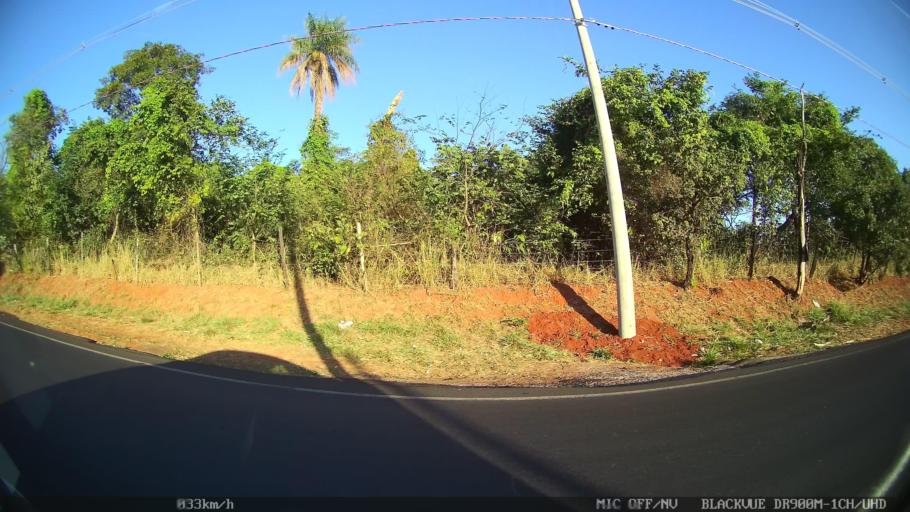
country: BR
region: Sao Paulo
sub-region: Sao Jose Do Rio Preto
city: Sao Jose do Rio Preto
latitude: -20.7673
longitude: -49.3554
